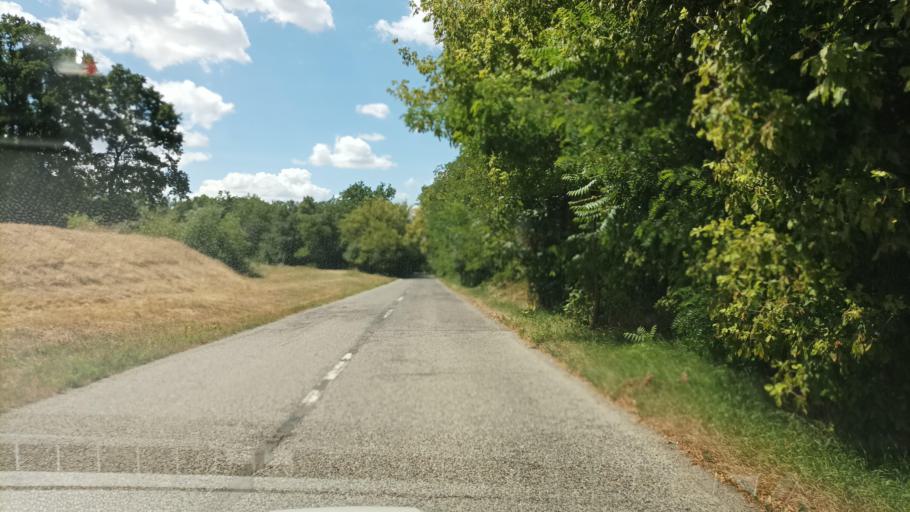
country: HU
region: Pest
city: Szentendre
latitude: 47.6748
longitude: 19.0897
